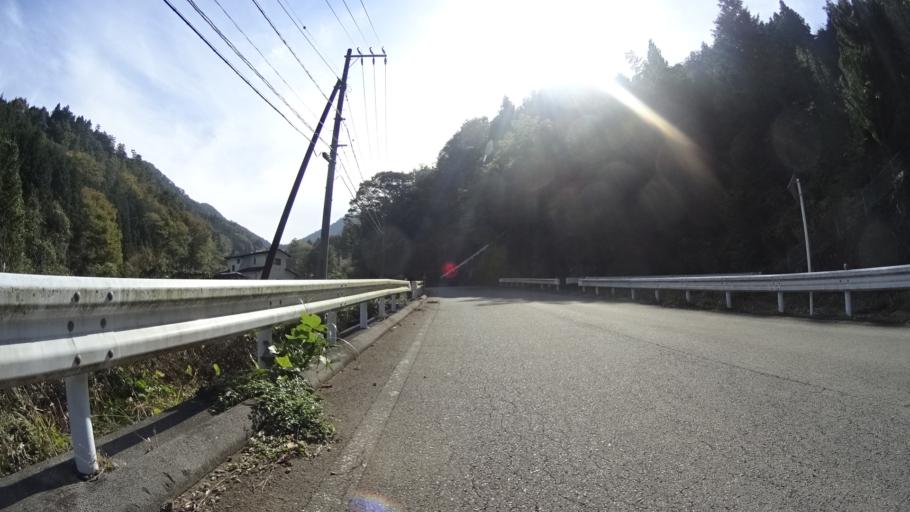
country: JP
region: Yamanashi
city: Otsuki
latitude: 35.5864
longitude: 138.9647
